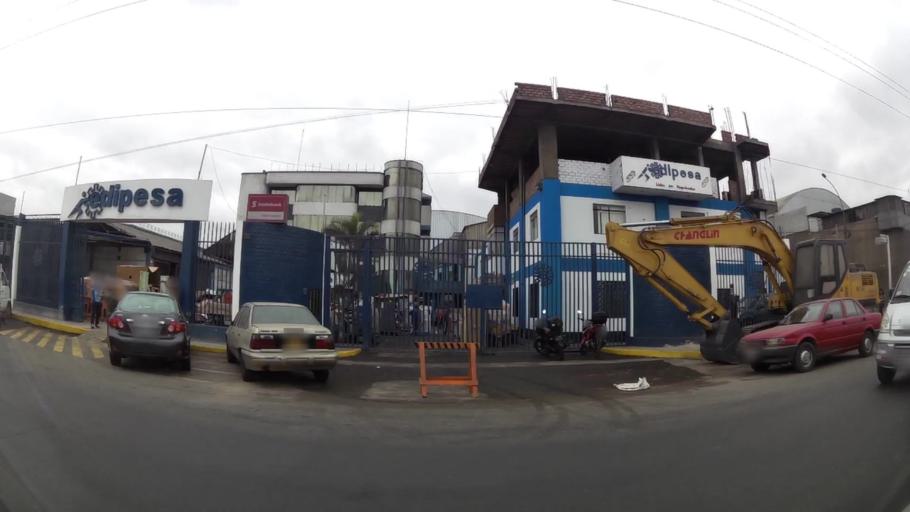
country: PE
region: Lima
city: Lima
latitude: -12.0454
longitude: -77.0639
